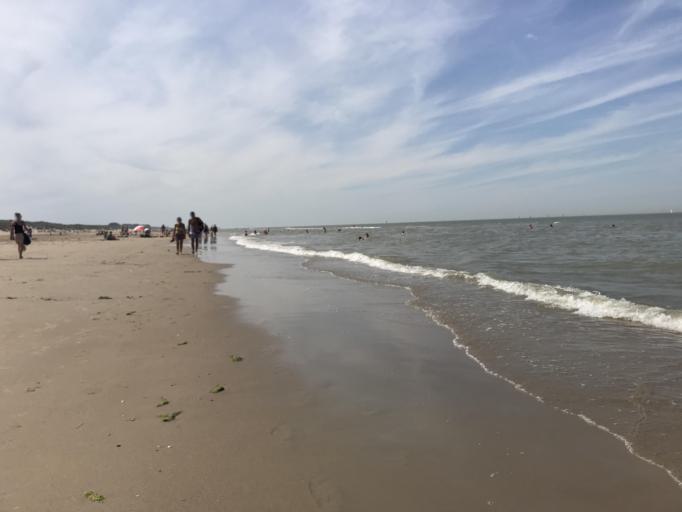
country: BE
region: Flanders
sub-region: Provincie West-Vlaanderen
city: De Haan
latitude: 51.2907
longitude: 3.0541
